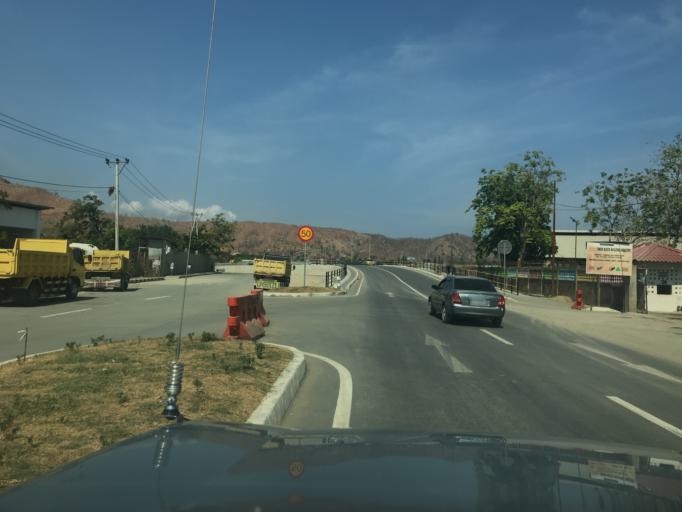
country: TL
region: Dili
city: Dili
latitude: -8.5609
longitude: 125.5363
